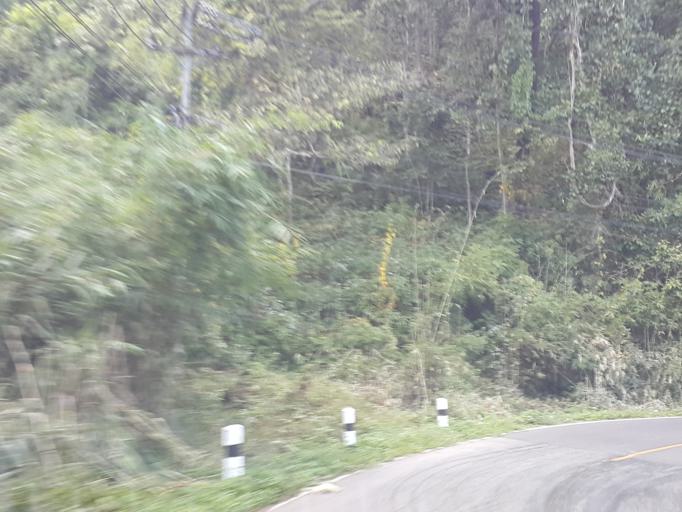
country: TH
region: Chiang Mai
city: Mae On
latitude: 18.9059
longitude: 99.2516
